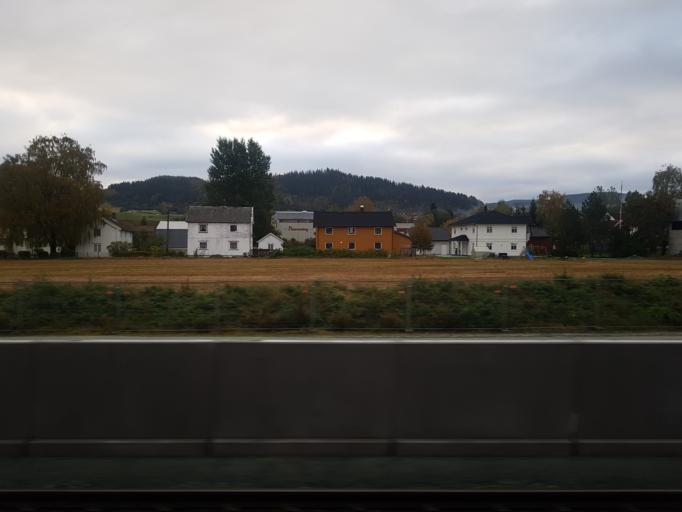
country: NO
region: Sor-Trondelag
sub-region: Melhus
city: Lundamo
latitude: 63.2046
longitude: 10.3042
